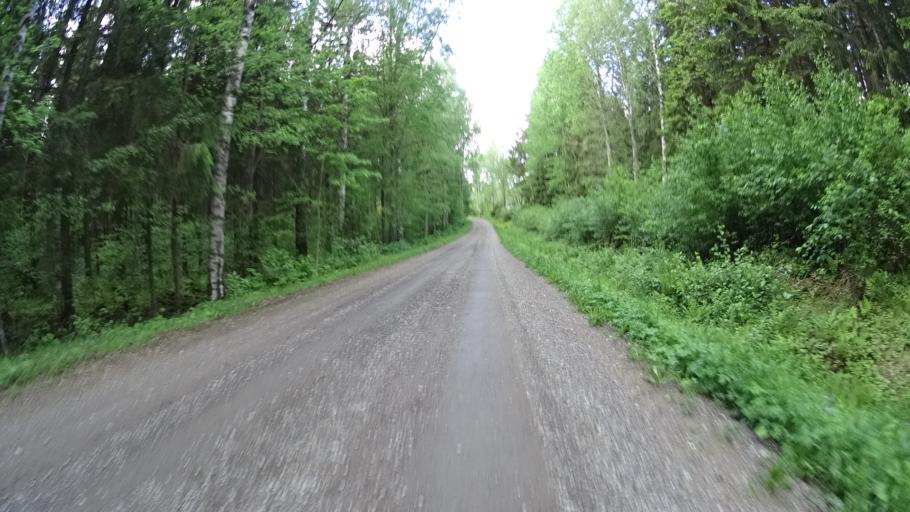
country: FI
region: Uusimaa
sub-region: Raaseporin
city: Pohja
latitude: 60.1689
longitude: 23.5994
